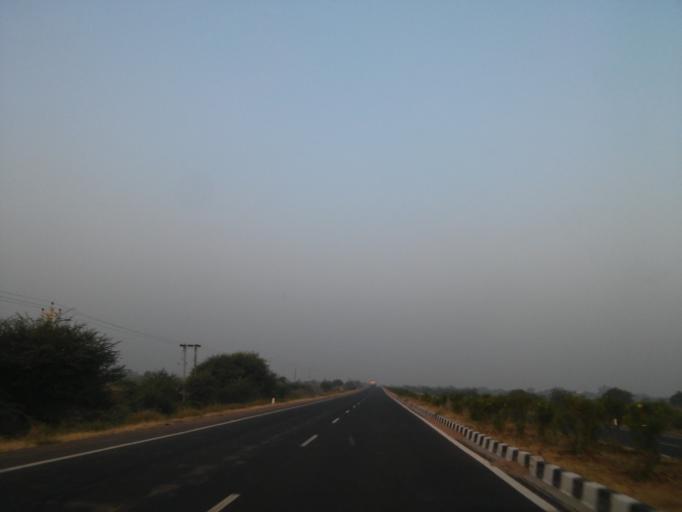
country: IN
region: Gujarat
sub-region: Surendranagar
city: Halvad
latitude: 23.0304
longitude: 70.9545
